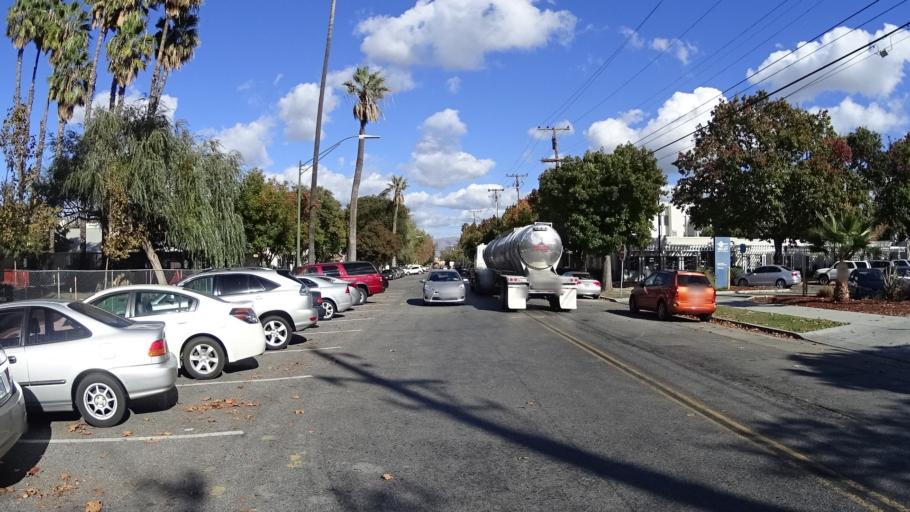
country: US
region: California
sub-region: Santa Clara County
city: Buena Vista
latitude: 37.3342
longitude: -121.9128
